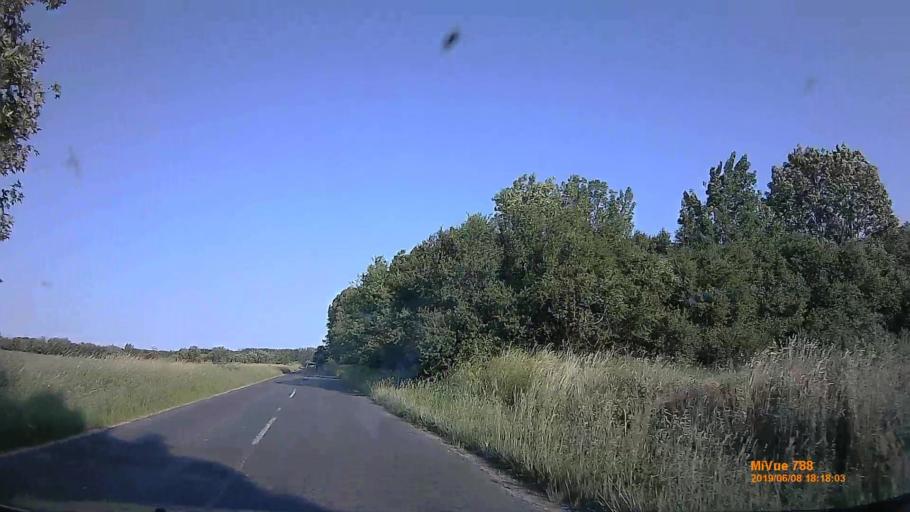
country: HU
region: Vas
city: Csepreg
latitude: 47.3772
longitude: 16.7228
